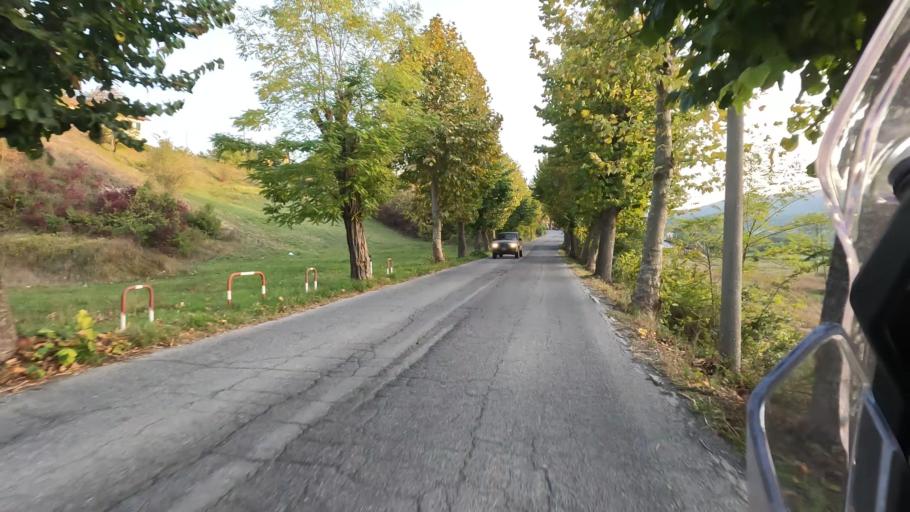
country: IT
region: Liguria
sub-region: Provincia di Savona
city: Mioglia
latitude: 44.4869
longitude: 8.4113
